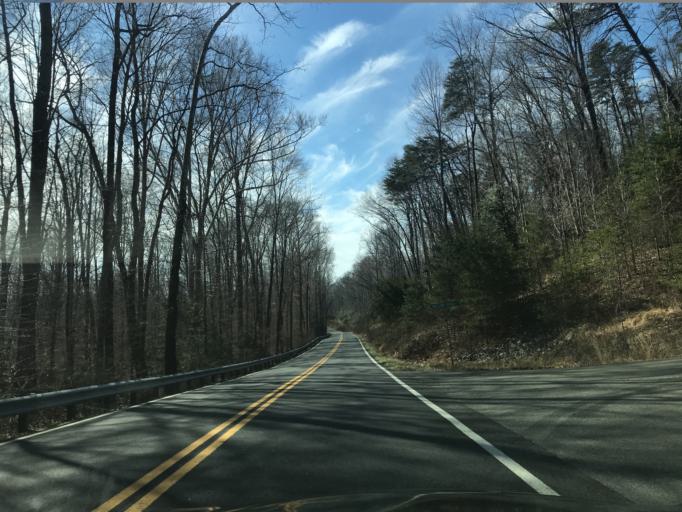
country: US
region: Maryland
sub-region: Charles County
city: Indian Head
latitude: 38.5113
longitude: -77.1482
